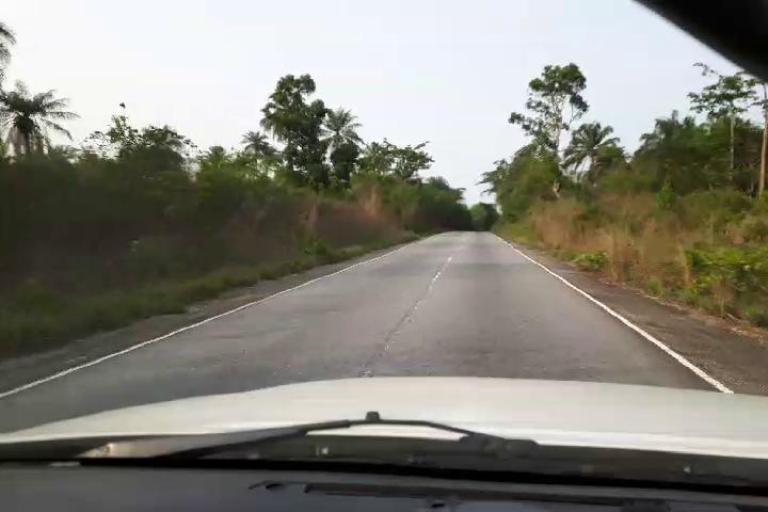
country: SL
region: Southern Province
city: Palima
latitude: 7.9312
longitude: -11.5302
